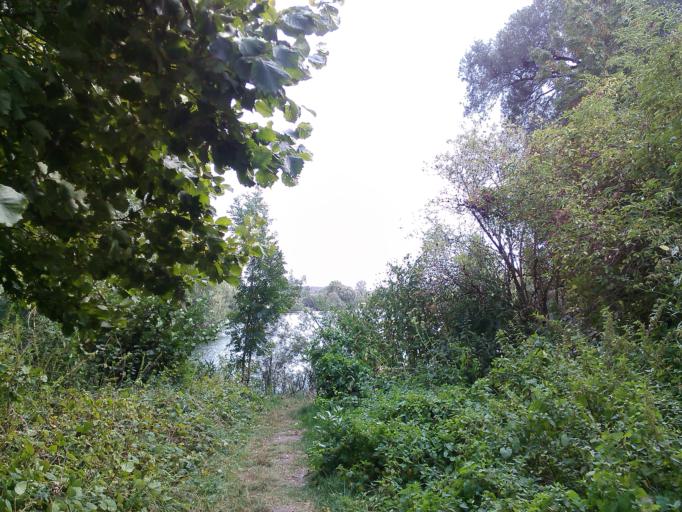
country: DE
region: Bavaria
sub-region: Upper Bavaria
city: Grobenzell
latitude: 48.1753
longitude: 11.3786
